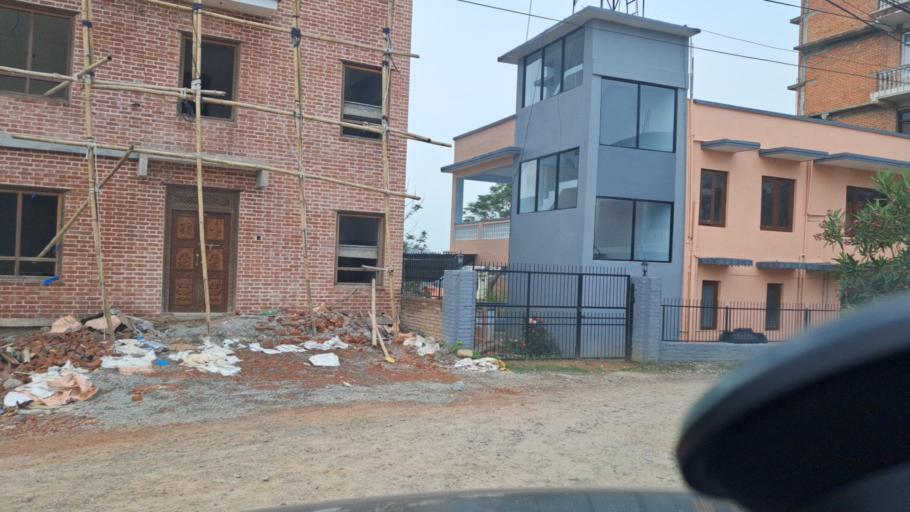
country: NP
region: Central Region
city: Banepa
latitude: 27.6155
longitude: 85.5529
